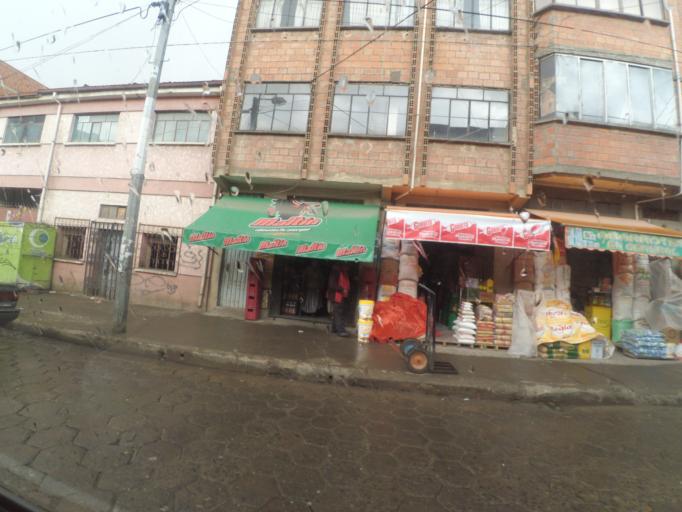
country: BO
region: La Paz
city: La Paz
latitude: -16.5129
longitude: -68.1643
